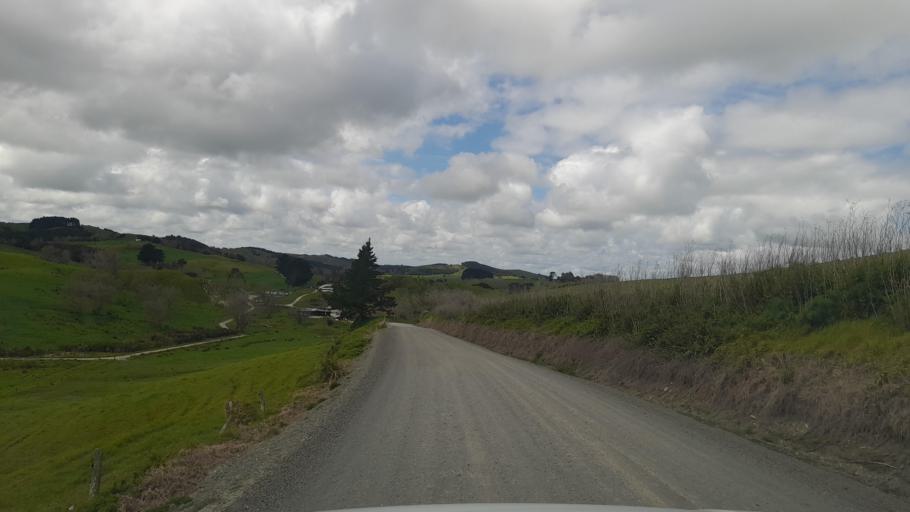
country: NZ
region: Auckland
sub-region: Auckland
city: Wellsford
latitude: -36.1545
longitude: 174.3081
